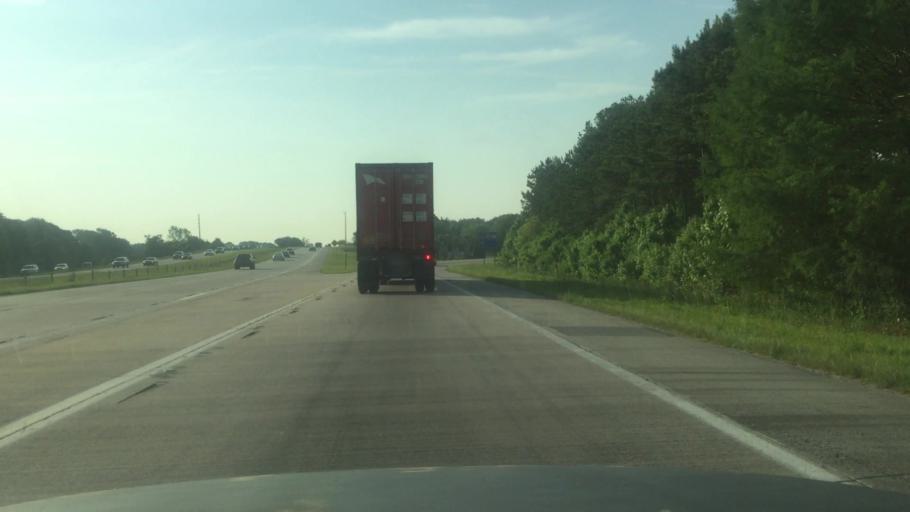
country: US
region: South Carolina
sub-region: Charleston County
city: Mount Pleasant
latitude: 32.8416
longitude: -79.8669
